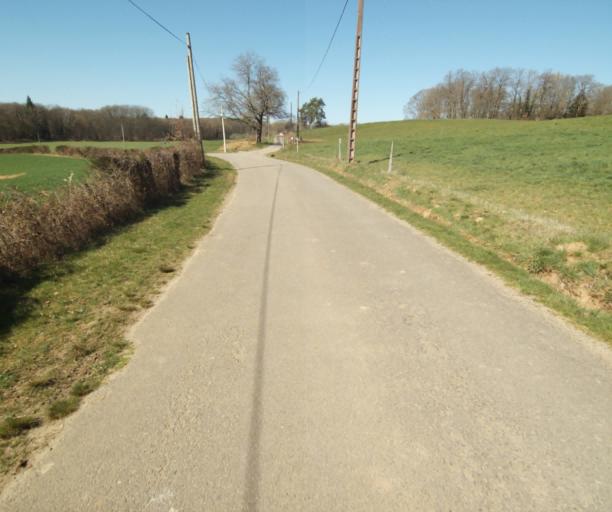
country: FR
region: Limousin
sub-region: Departement de la Correze
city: Saint-Clement
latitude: 45.3080
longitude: 1.7134
